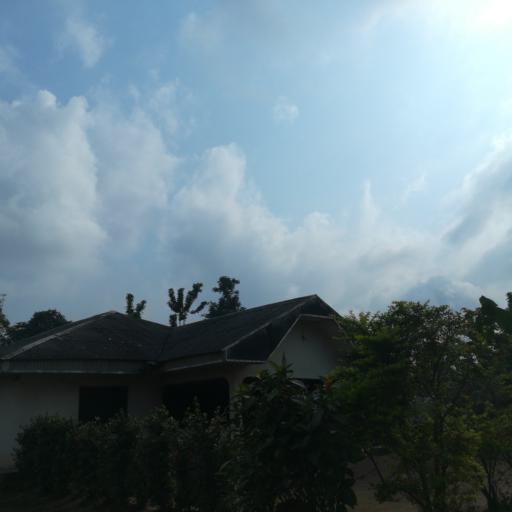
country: NG
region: Rivers
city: Okrika
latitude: 4.7813
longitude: 7.1457
